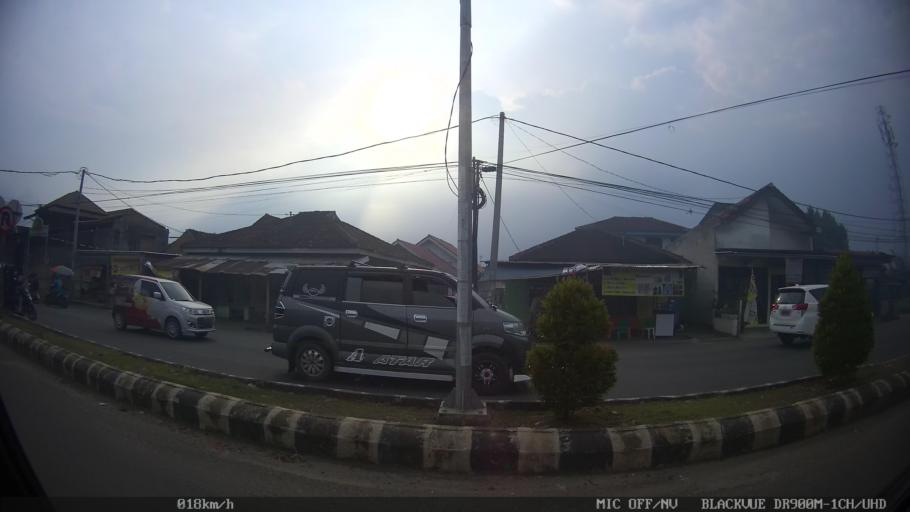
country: ID
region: Lampung
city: Kedaton
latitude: -5.3610
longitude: 105.2353
